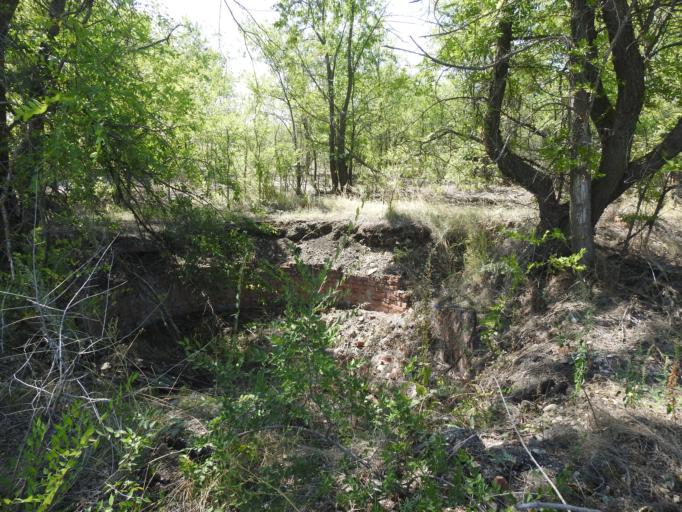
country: RU
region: Saratov
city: Engel's
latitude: 51.4347
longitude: 46.2263
